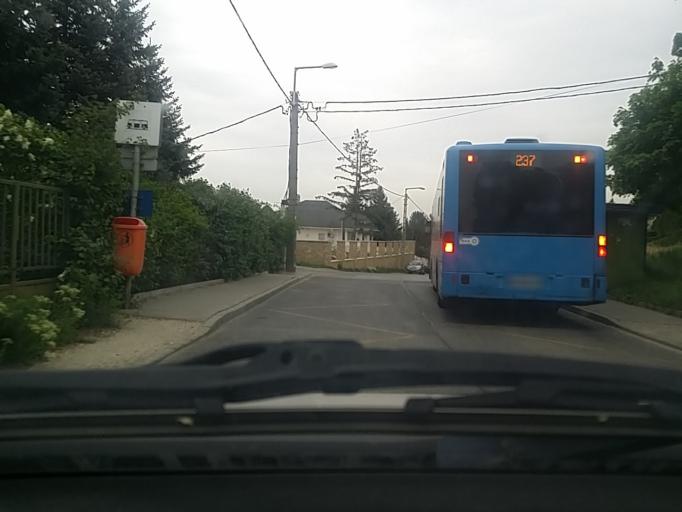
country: HU
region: Budapest
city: Budapest III. keruelet
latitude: 47.5578
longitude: 19.0153
